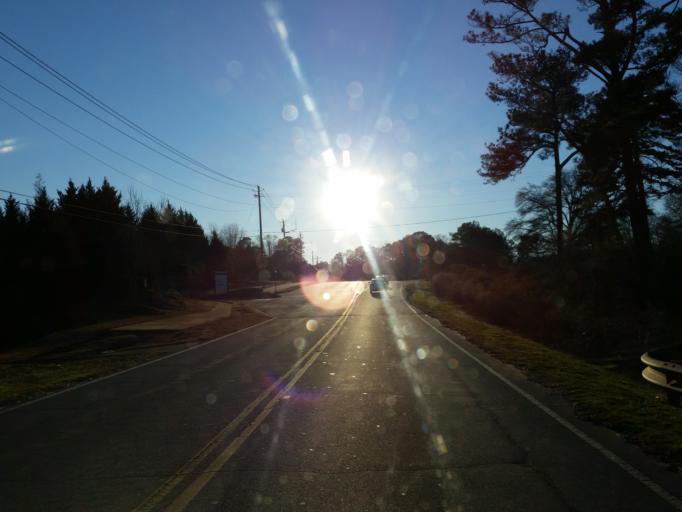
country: US
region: Georgia
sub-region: Cherokee County
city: Woodstock
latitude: 34.1163
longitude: -84.5105
